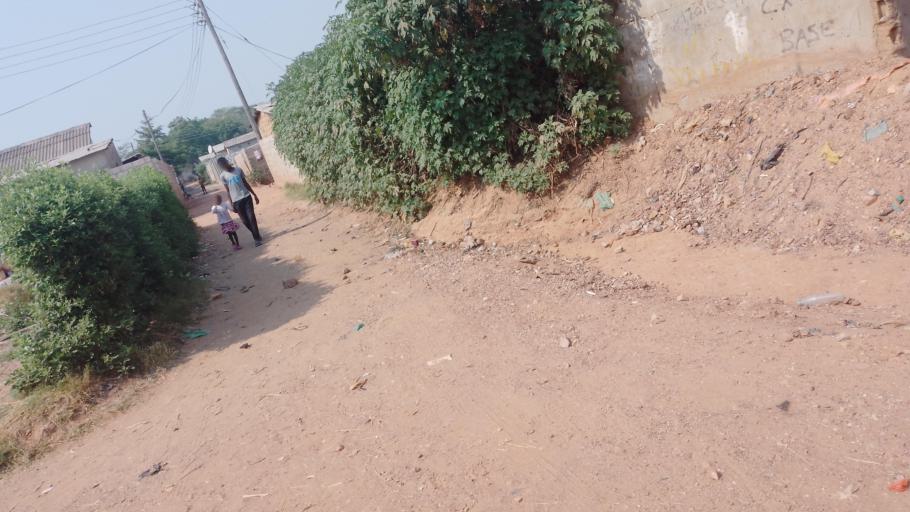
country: ZM
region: Lusaka
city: Lusaka
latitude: -15.4007
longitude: 28.3659
